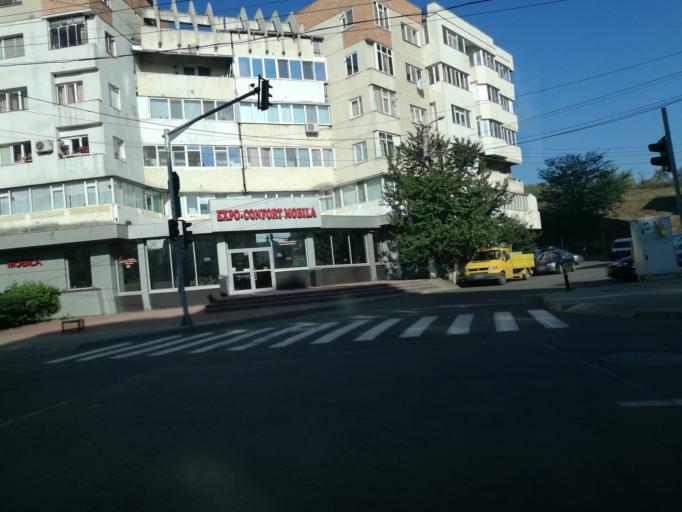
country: RO
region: Iasi
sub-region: Comuna Miroslava
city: Miroslava
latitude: 47.1744
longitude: 27.5411
